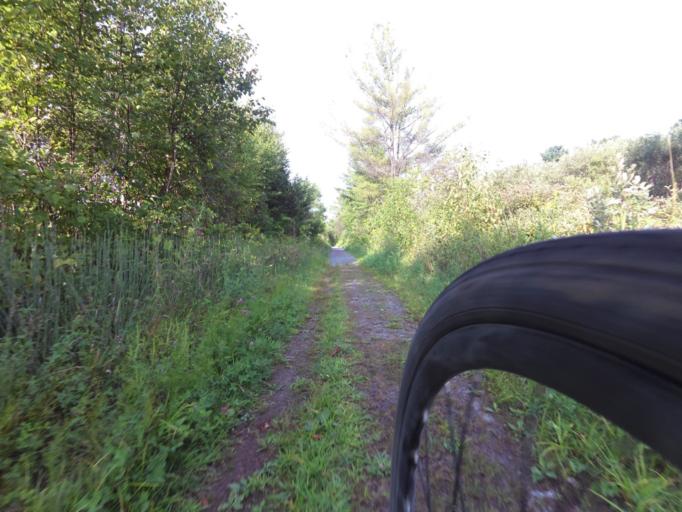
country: CA
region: Ontario
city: Kingston
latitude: 44.4718
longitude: -76.4932
